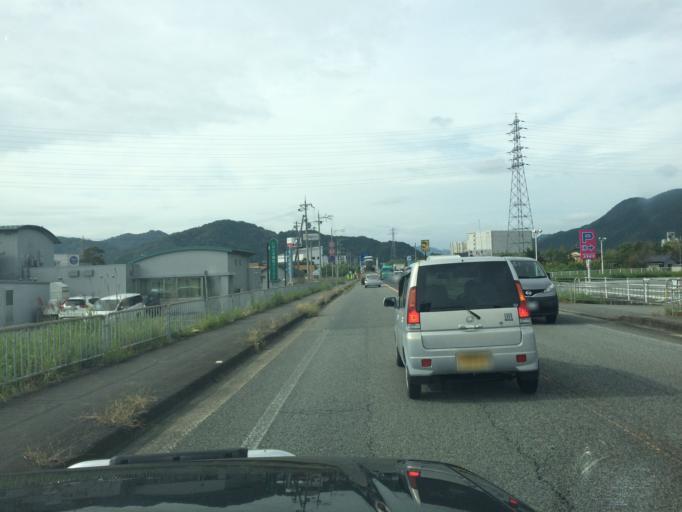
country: JP
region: Hyogo
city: Toyooka
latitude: 35.3295
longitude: 134.8673
